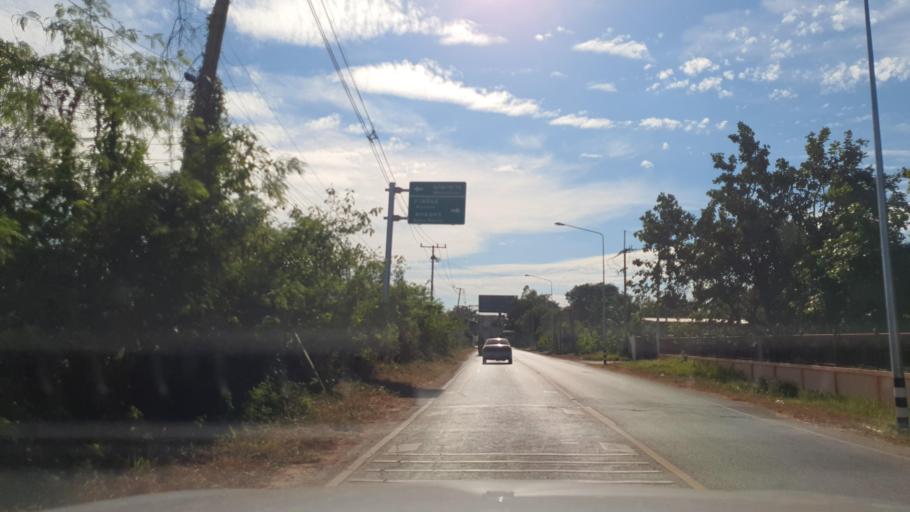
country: TH
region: Kalasin
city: Kuchinarai
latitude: 16.5352
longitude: 104.0746
